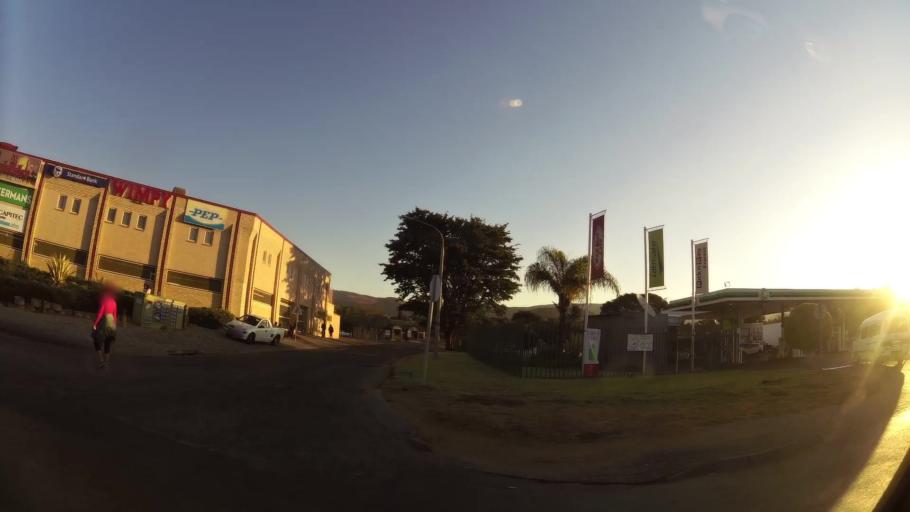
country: ZA
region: North-West
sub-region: Bojanala Platinum District Municipality
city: Rustenburg
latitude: -25.6929
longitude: 27.2245
